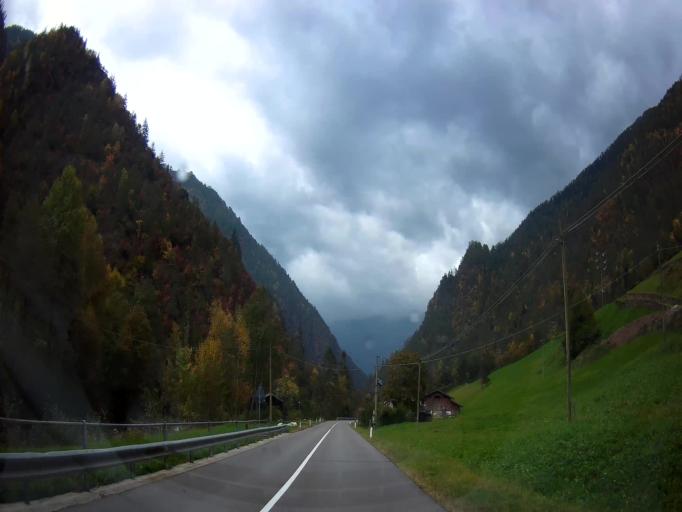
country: IT
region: Trentino-Alto Adige
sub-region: Bolzano
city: Certosa
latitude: 46.6757
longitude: 10.9391
